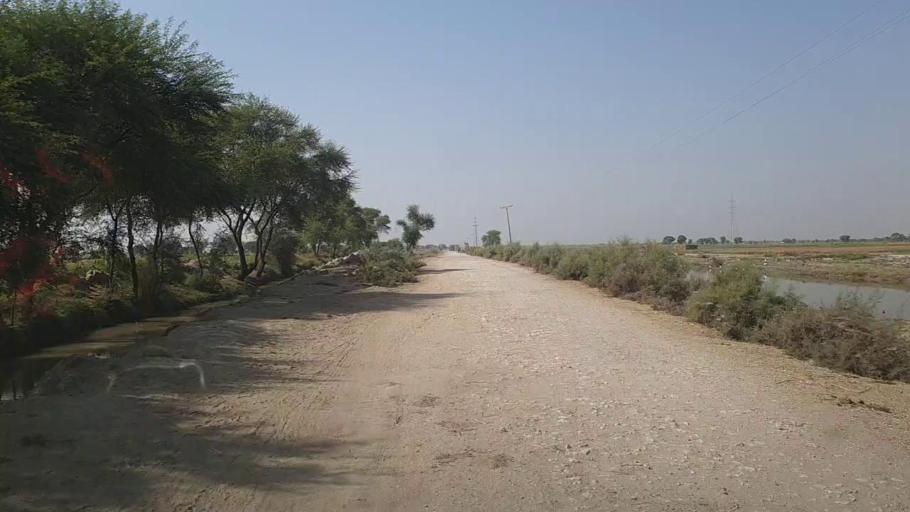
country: PK
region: Sindh
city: Kandhkot
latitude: 28.4068
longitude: 69.2520
